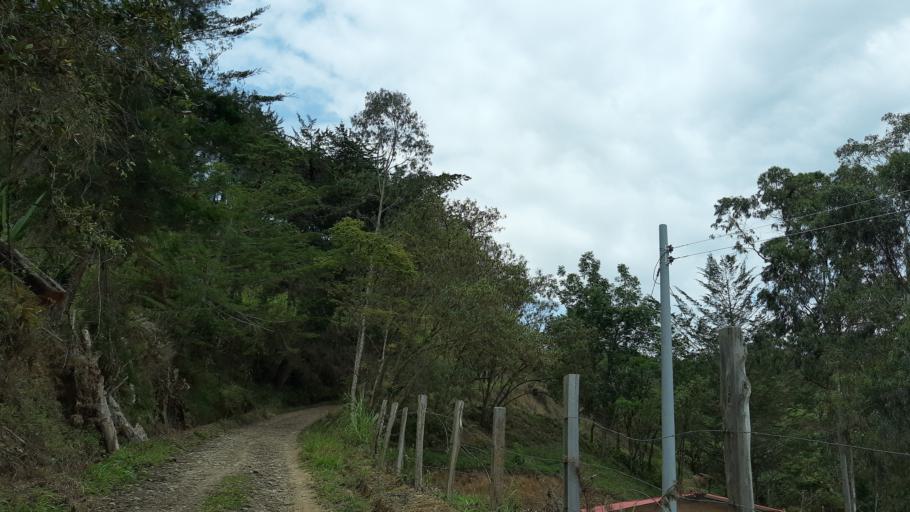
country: CO
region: Boyaca
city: Garagoa
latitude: 5.0637
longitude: -73.3619
